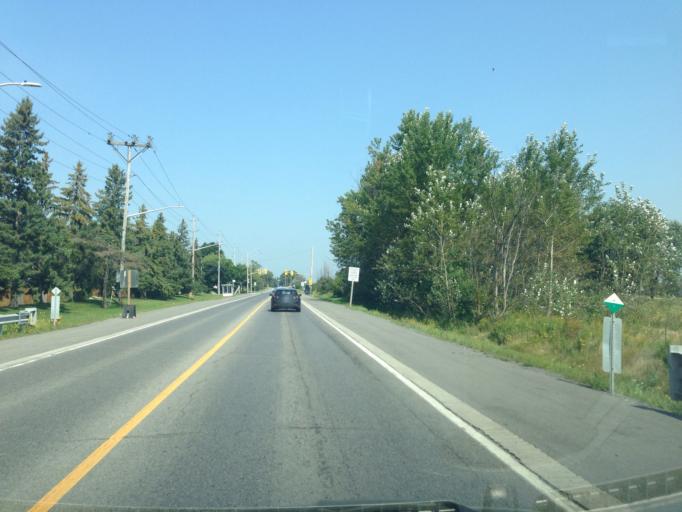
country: CA
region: Ontario
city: Ottawa
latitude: 45.4217
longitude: -75.5969
